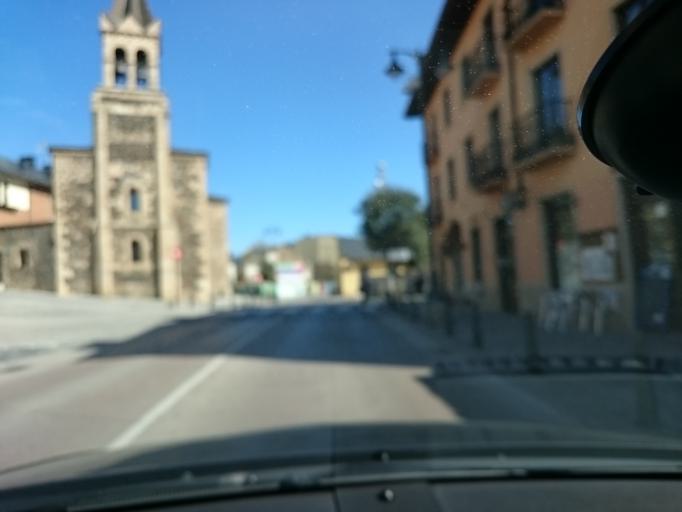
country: ES
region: Castille and Leon
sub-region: Provincia de Leon
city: Ponferrada
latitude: 42.5430
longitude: -6.5937
